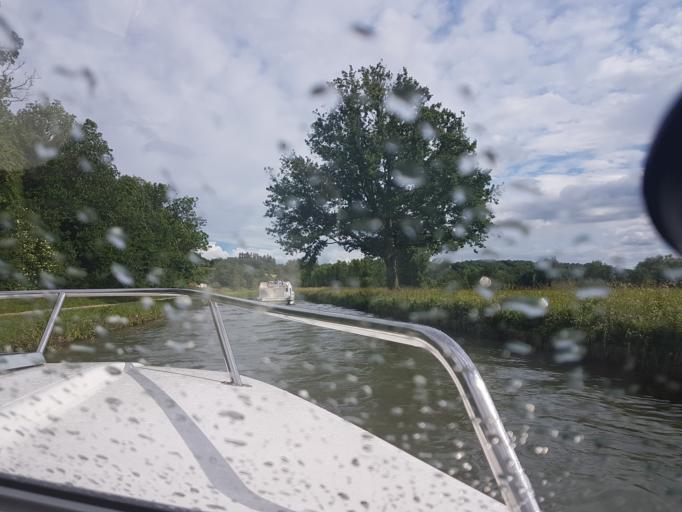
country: FR
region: Bourgogne
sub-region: Departement de la Nievre
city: Clamecy
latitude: 47.5422
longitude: 3.6337
